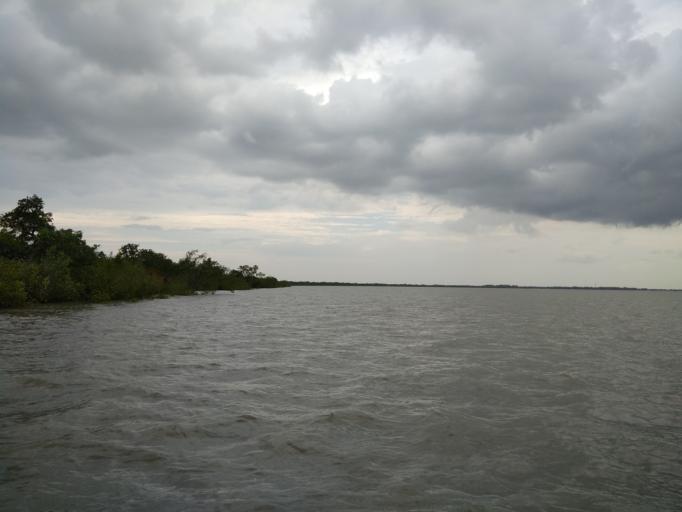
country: IN
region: West Bengal
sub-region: North 24 Parganas
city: Gosaba
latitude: 22.2190
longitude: 89.2409
